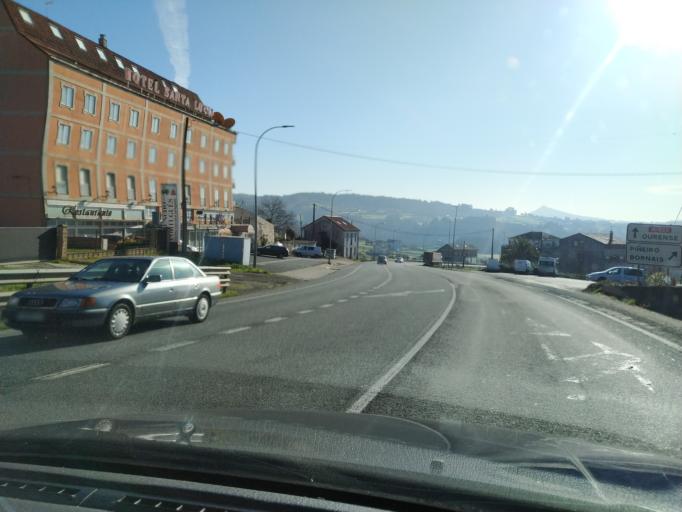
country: ES
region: Galicia
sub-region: Provincia da Coruna
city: Santiago de Compostela
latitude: 42.8526
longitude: -8.5278
